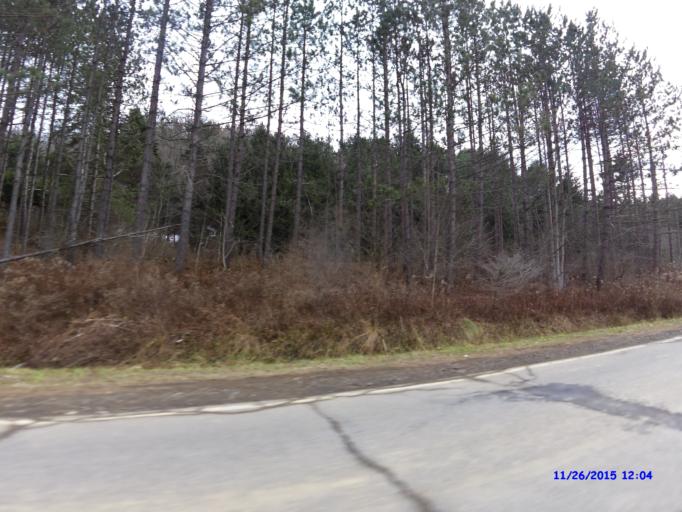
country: US
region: New York
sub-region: Cattaraugus County
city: Franklinville
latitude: 42.2334
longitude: -78.4421
